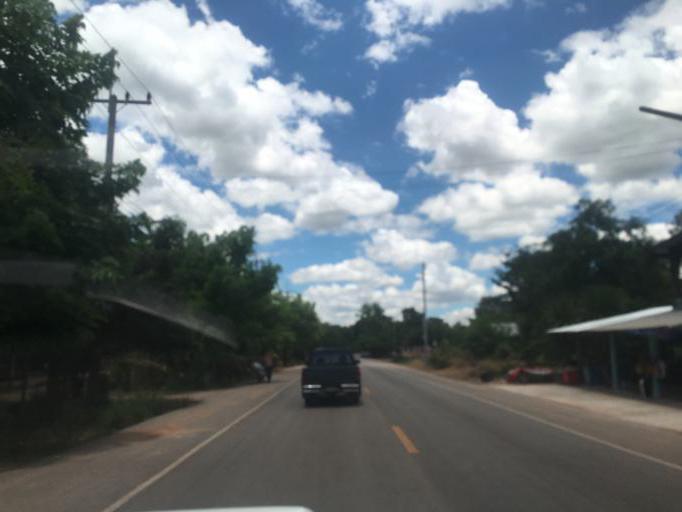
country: TH
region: Changwat Udon Thani
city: Nong Saeng
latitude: 17.1560
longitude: 102.7874
